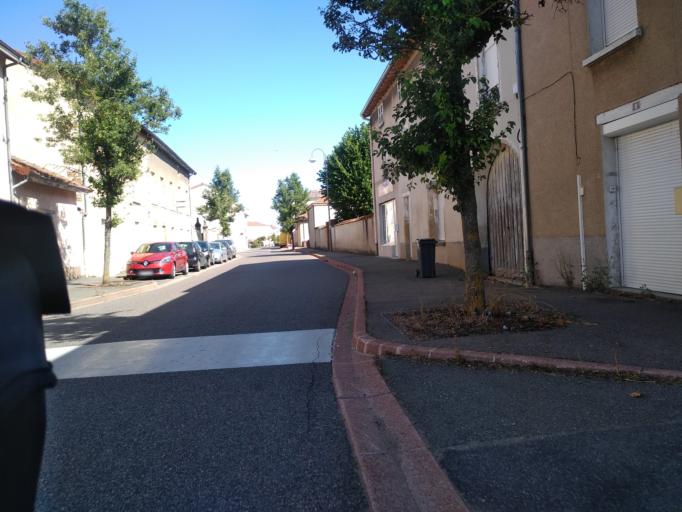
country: FR
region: Rhone-Alpes
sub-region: Departement de la Loire
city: Neulise
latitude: 45.9011
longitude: 4.1814
